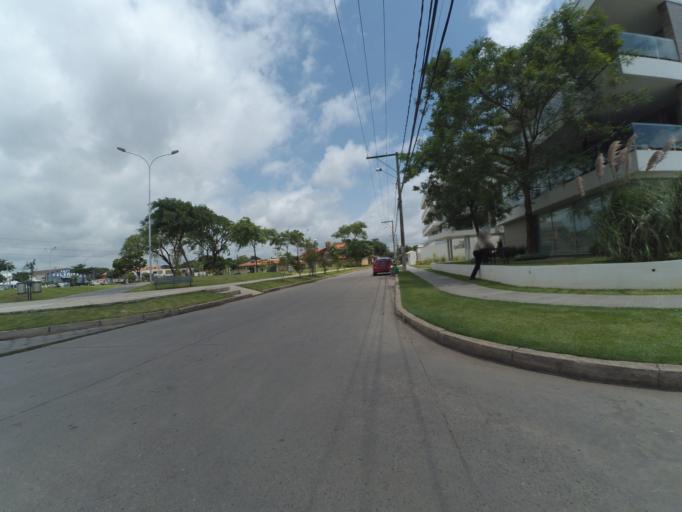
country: BO
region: Santa Cruz
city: Santa Cruz de la Sierra
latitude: -17.8047
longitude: -63.2121
